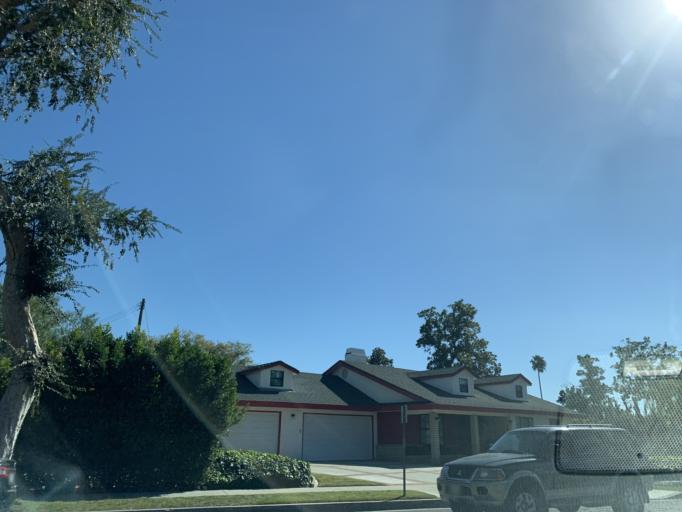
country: US
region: California
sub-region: Orange County
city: Placentia
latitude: 33.8813
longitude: -117.8960
